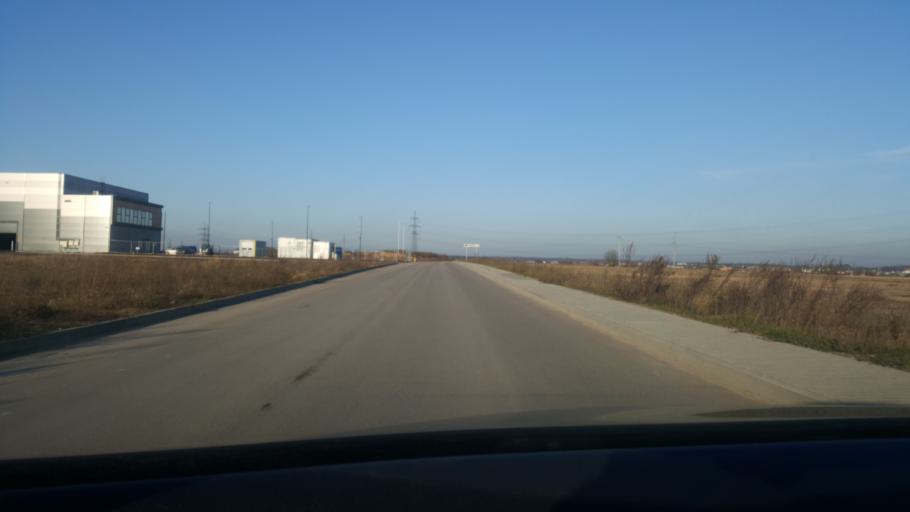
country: LT
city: Ramuciai
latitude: 54.9325
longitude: 24.0352
